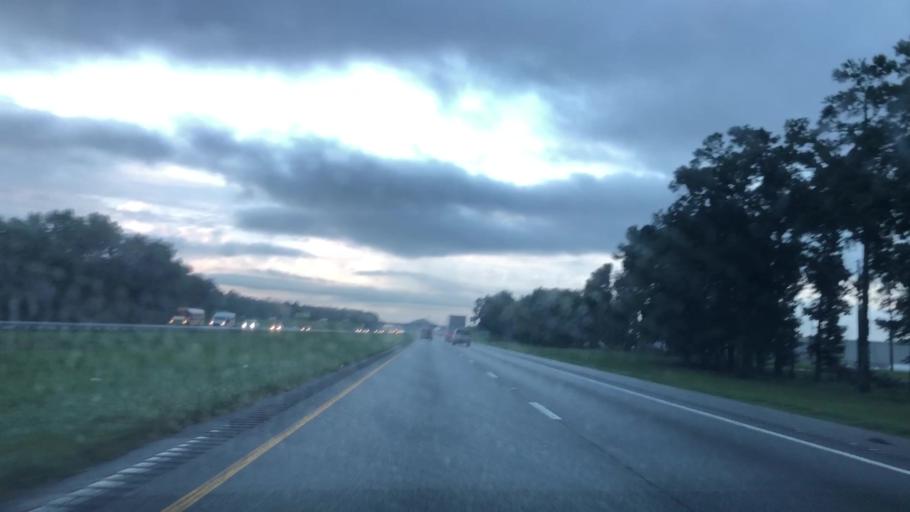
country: US
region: Alabama
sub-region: Shelby County
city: Alabaster
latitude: 33.1781
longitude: -86.7800
